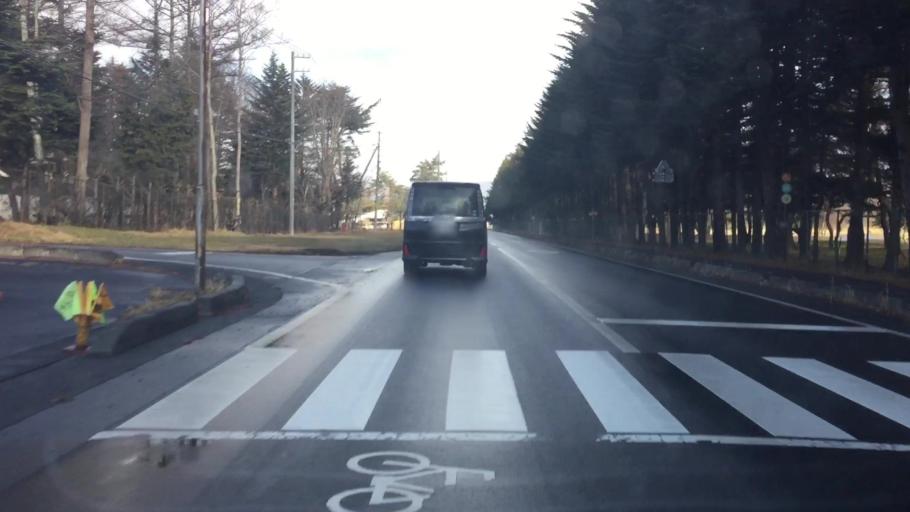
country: JP
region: Nagano
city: Saku
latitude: 36.3077
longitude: 138.6317
